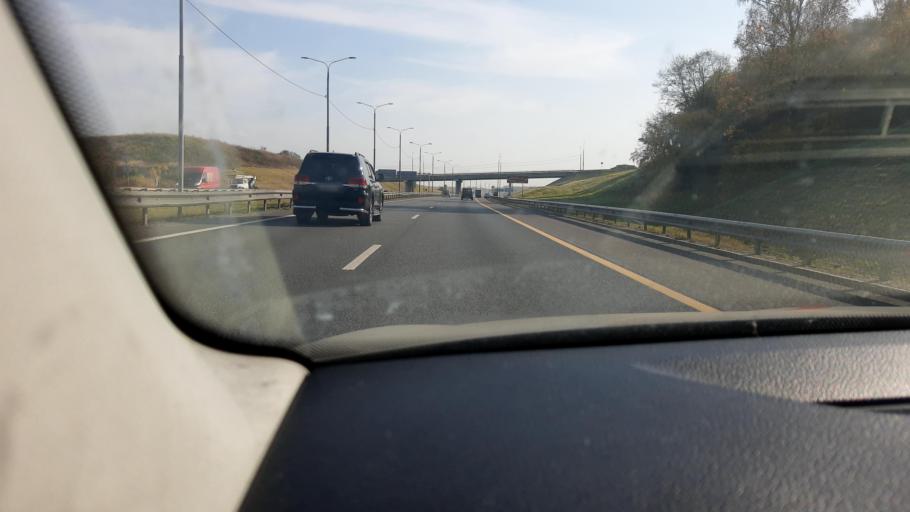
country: RU
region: Moskovskaya
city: Stupino
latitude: 54.8118
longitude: 38.0635
